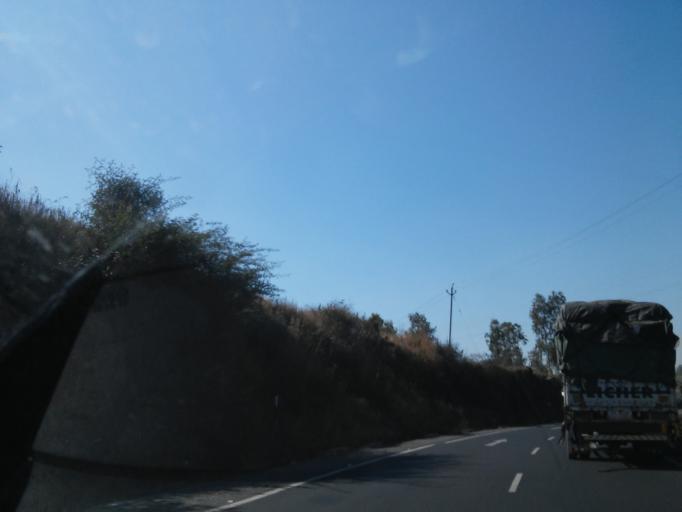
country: IN
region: Gujarat
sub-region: Sabar Kantha
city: Meghraj
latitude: 23.7405
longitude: 73.4328
